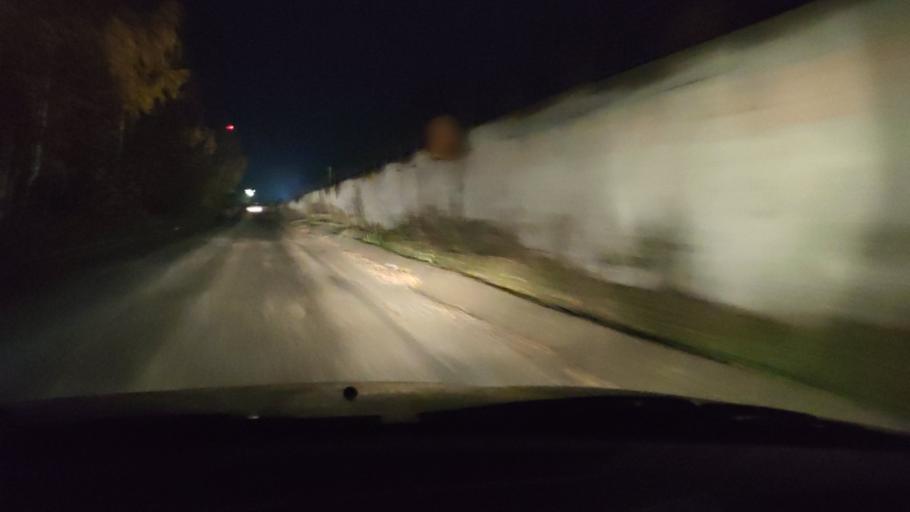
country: RU
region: Perm
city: Overyata
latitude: 58.0266
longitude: 55.9202
